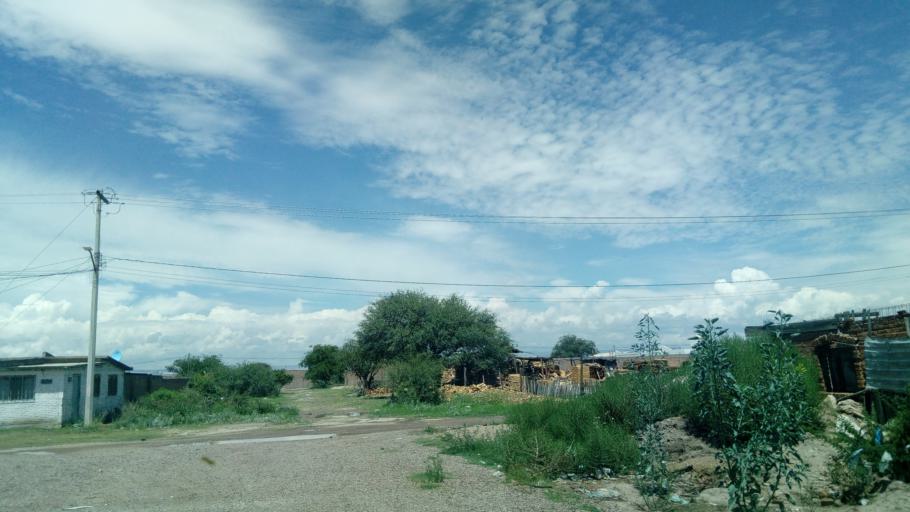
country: MX
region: Durango
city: Victoria de Durango
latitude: 24.0146
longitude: -104.5895
